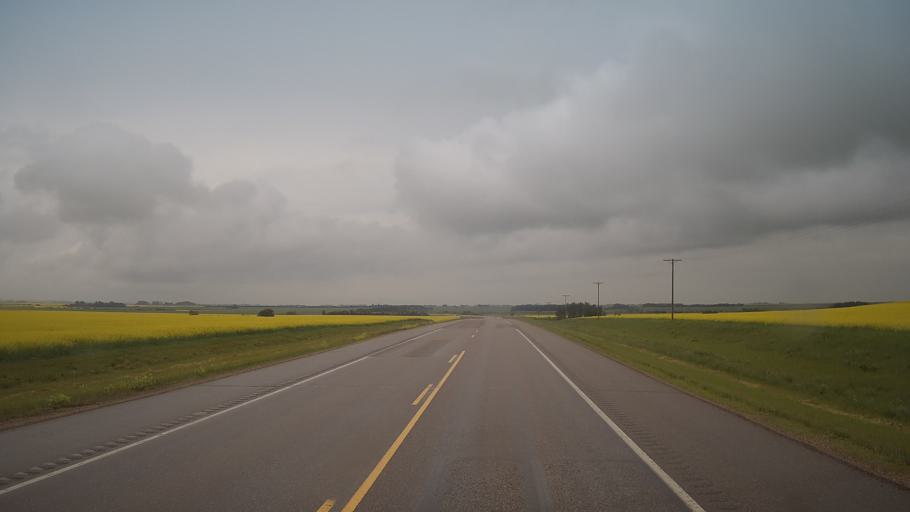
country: CA
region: Saskatchewan
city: Wilkie
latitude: 52.4300
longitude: -108.9184
